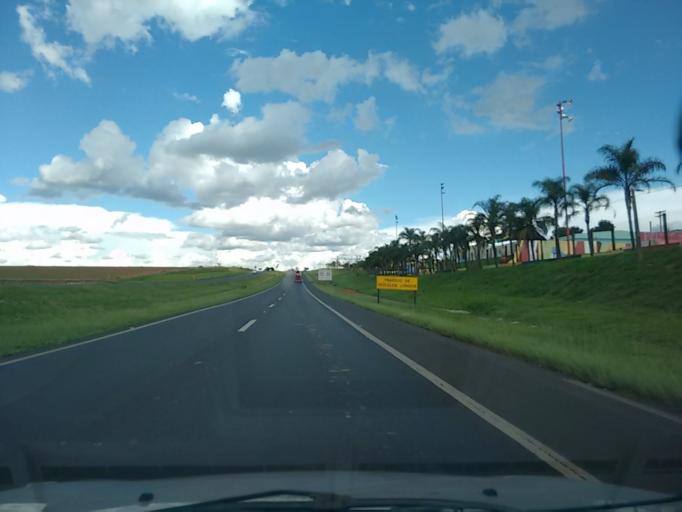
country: BR
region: Sao Paulo
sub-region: Ibate
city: Ibate
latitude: -21.9523
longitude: -47.9907
